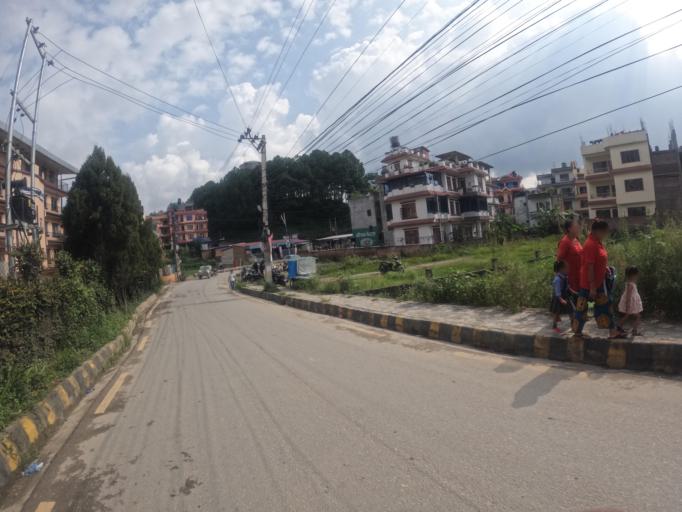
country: NP
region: Central Region
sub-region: Bagmati Zone
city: Bhaktapur
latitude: 27.6643
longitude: 85.3860
